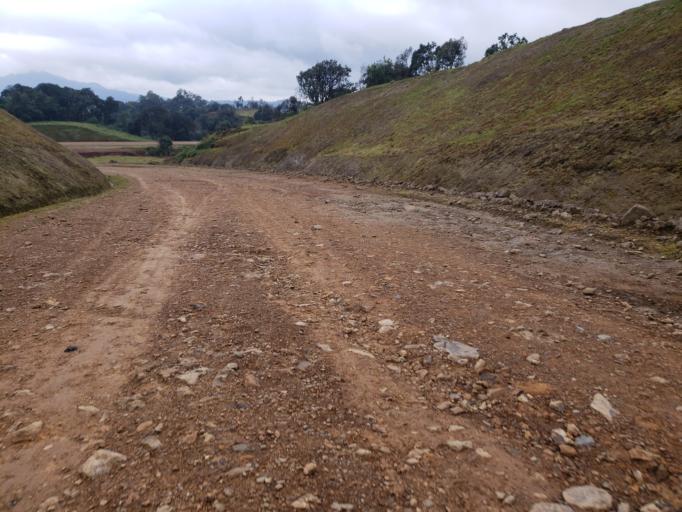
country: ET
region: Oromiya
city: Dodola
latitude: 6.6821
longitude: 39.3658
